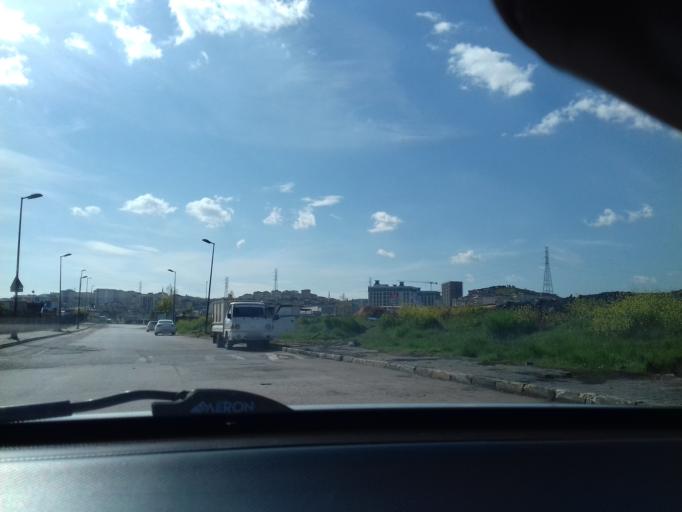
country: TR
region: Istanbul
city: Pendik
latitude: 40.9008
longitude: 29.2774
